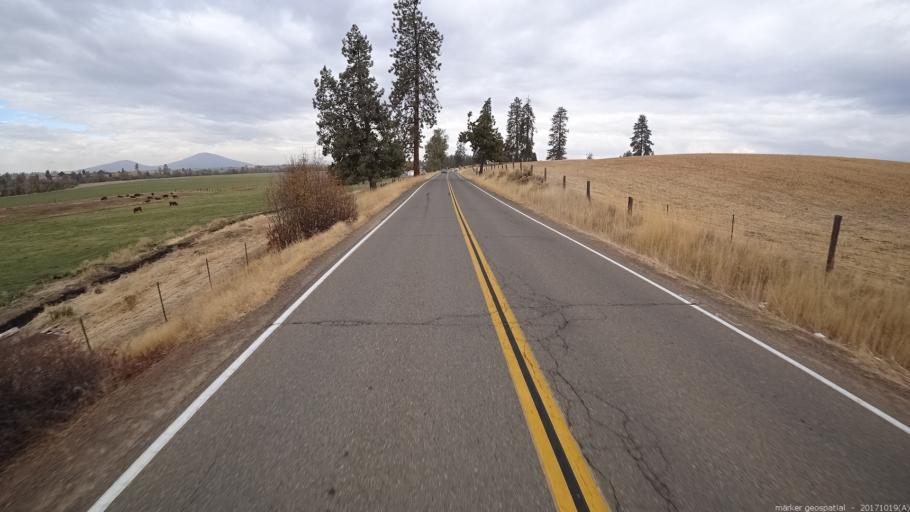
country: US
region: California
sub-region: Shasta County
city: Burney
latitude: 41.0527
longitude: -121.3536
